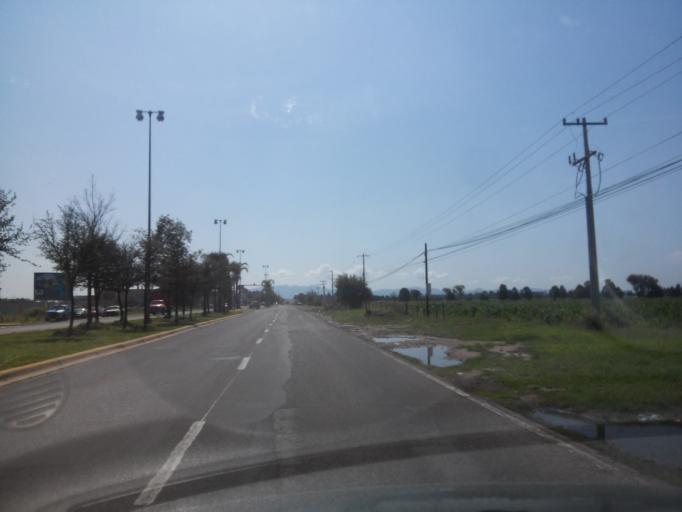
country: MX
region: Durango
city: Victoria de Durango
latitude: 23.9942
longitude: -104.6322
